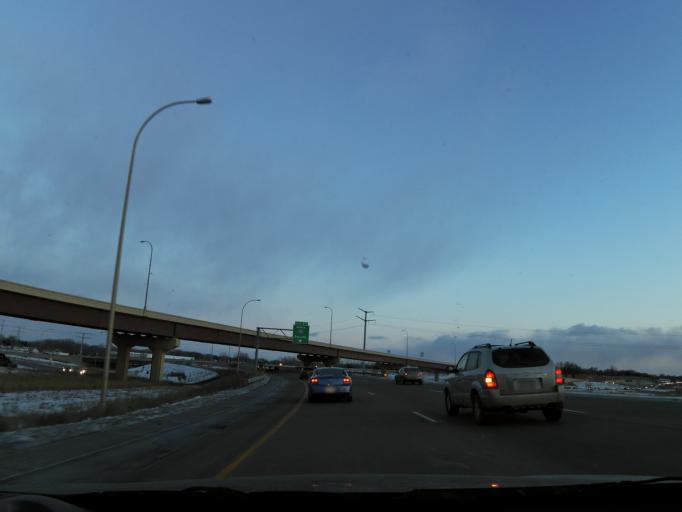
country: US
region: Minnesota
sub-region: Ramsey County
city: Little Canada
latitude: 45.0365
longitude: -93.0909
